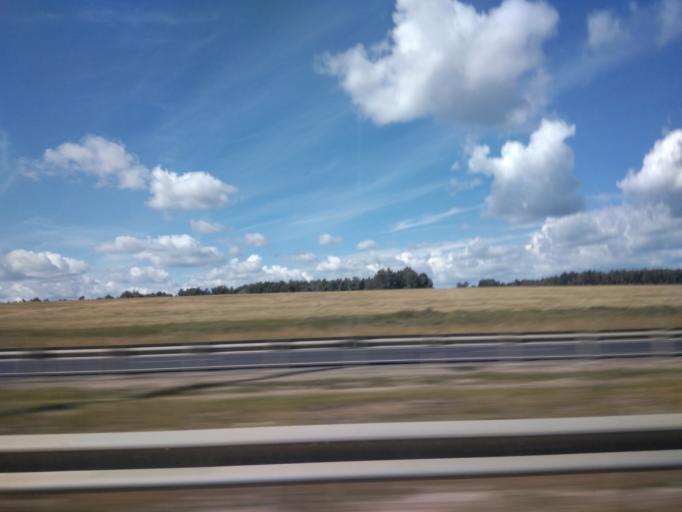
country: RU
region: Tula
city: Zaokskiy
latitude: 54.8146
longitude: 37.4795
